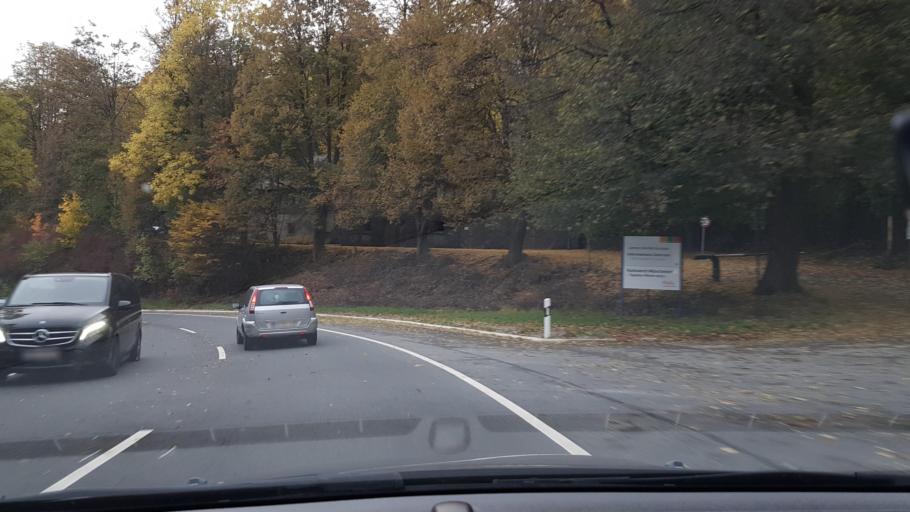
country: DE
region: Lower Saxony
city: Bad Grund
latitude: 51.8233
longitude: 10.2326
